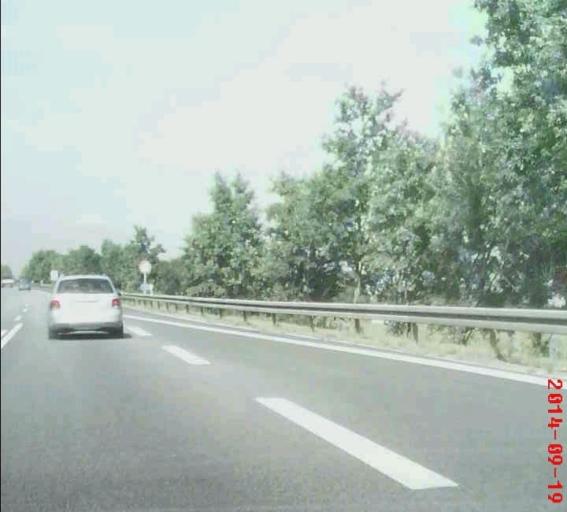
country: DE
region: Bavaria
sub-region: Upper Palatinate
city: Schirmitz
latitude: 49.6480
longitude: 12.1481
